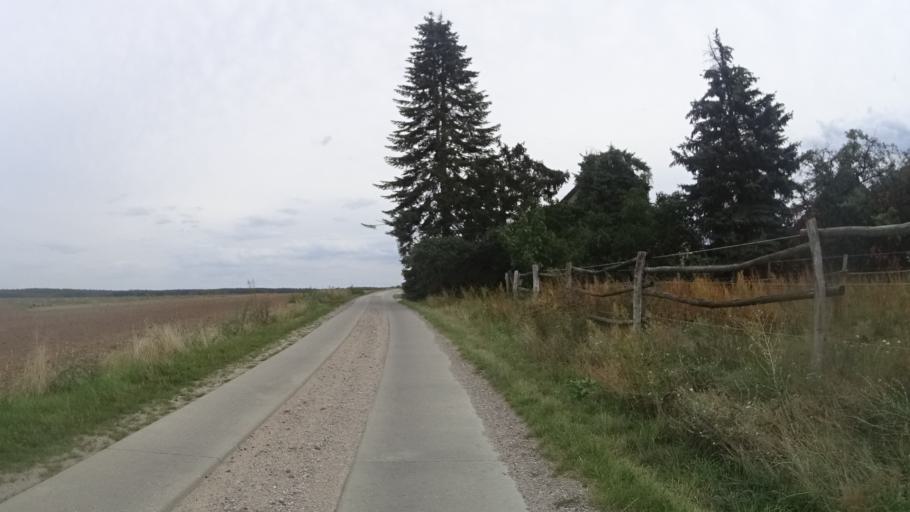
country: DE
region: Brandenburg
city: Beelitz
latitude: 52.1766
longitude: 12.9823
